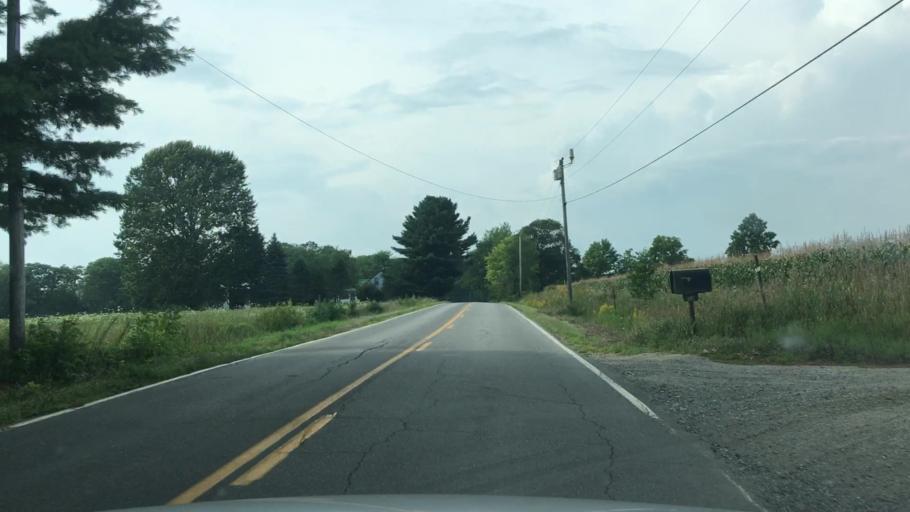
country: US
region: Maine
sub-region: Knox County
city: Washington
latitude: 44.2152
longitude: -69.3843
